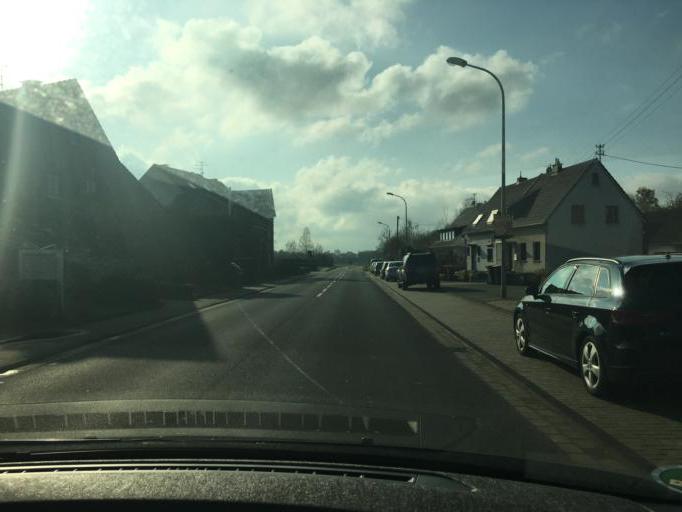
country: DE
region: North Rhine-Westphalia
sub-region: Regierungsbezirk Koln
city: Weilerswist
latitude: 50.7367
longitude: 6.8854
